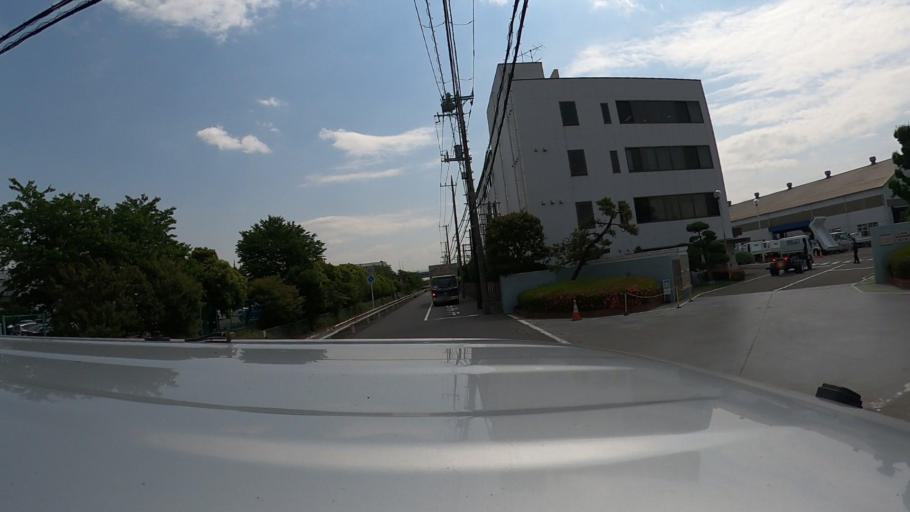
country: JP
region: Kanagawa
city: Chigasaki
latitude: 35.3573
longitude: 139.3729
